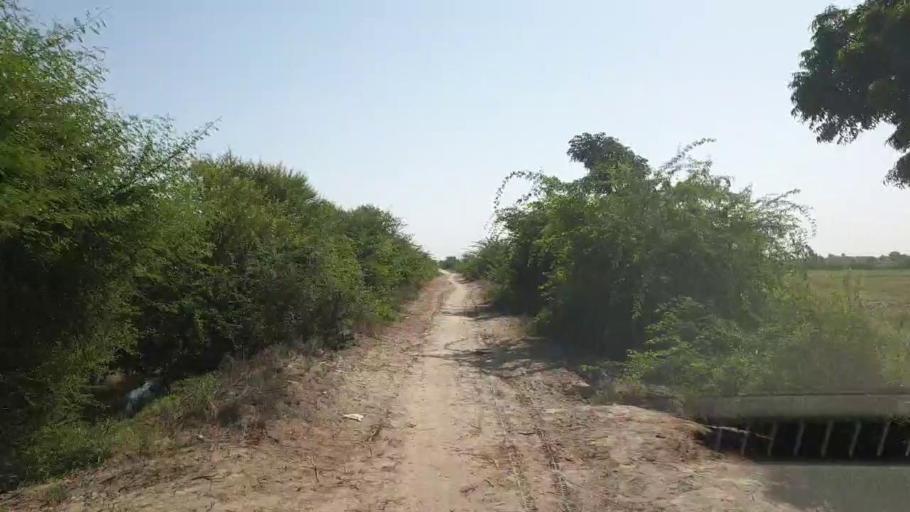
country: PK
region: Sindh
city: Kadhan
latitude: 24.6017
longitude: 69.0042
